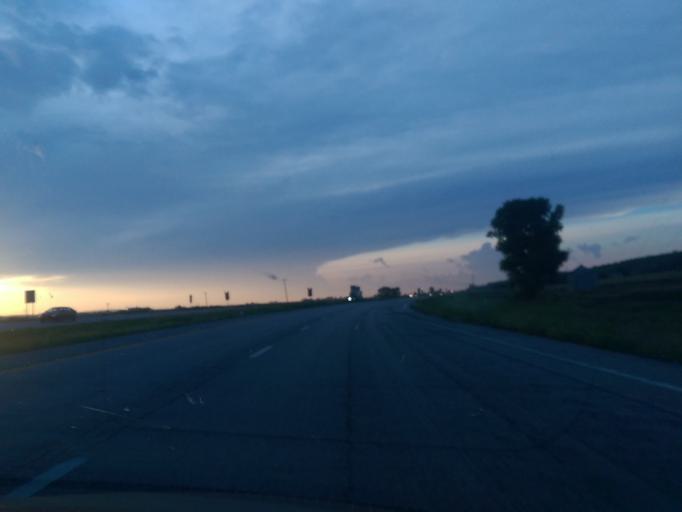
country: US
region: Missouri
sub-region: Atchison County
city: Rock Port
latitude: 40.3720
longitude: -95.5357
